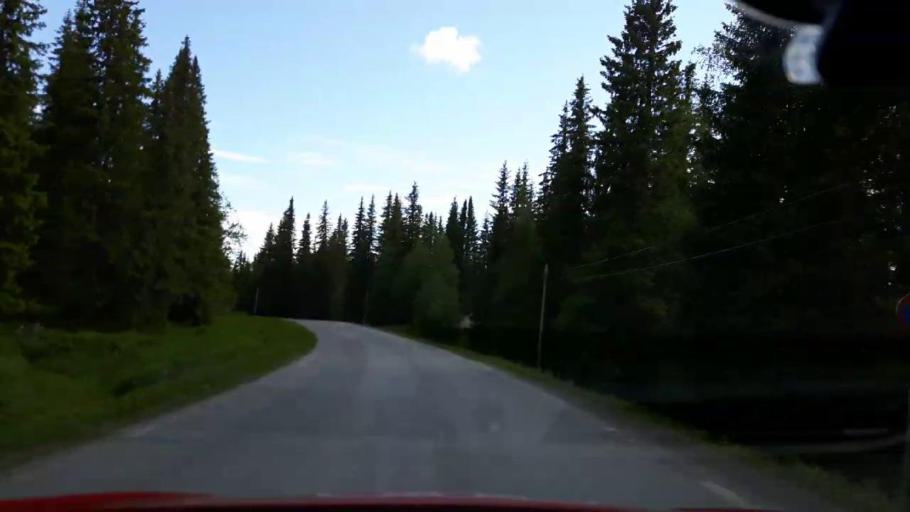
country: SE
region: Jaemtland
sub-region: Krokoms Kommun
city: Valla
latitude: 63.7788
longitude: 14.0436
